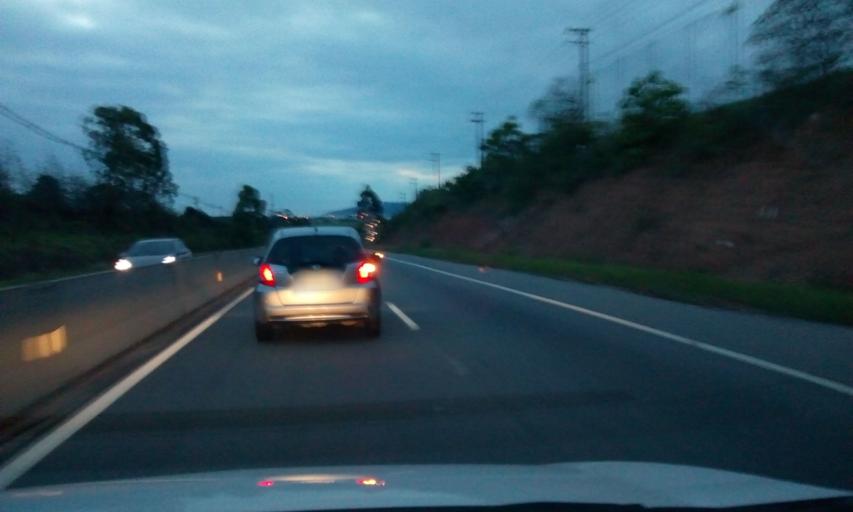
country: BR
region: Sao Paulo
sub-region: Itupeva
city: Itupeva
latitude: -23.1720
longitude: -46.9954
